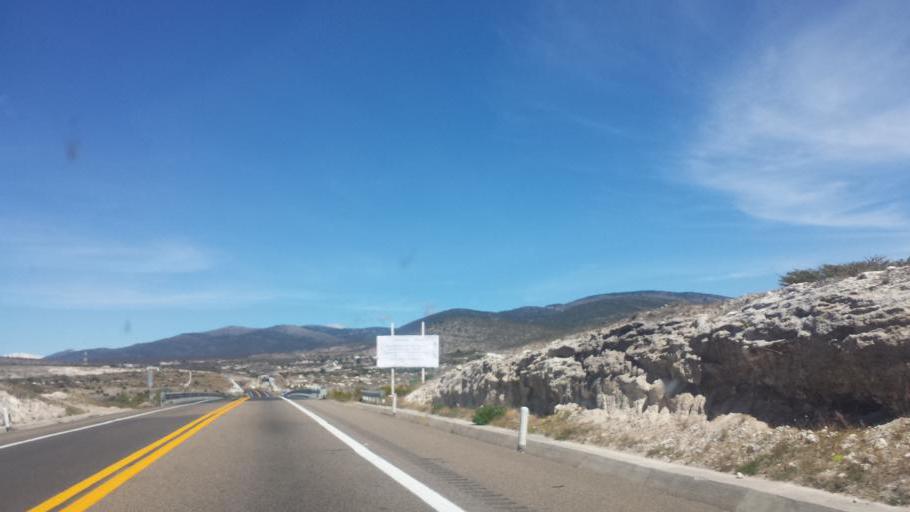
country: MX
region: Oaxaca
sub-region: Villa Tejupam de la Union
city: Villa Tejupam de la Union
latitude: 17.9181
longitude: -97.3610
